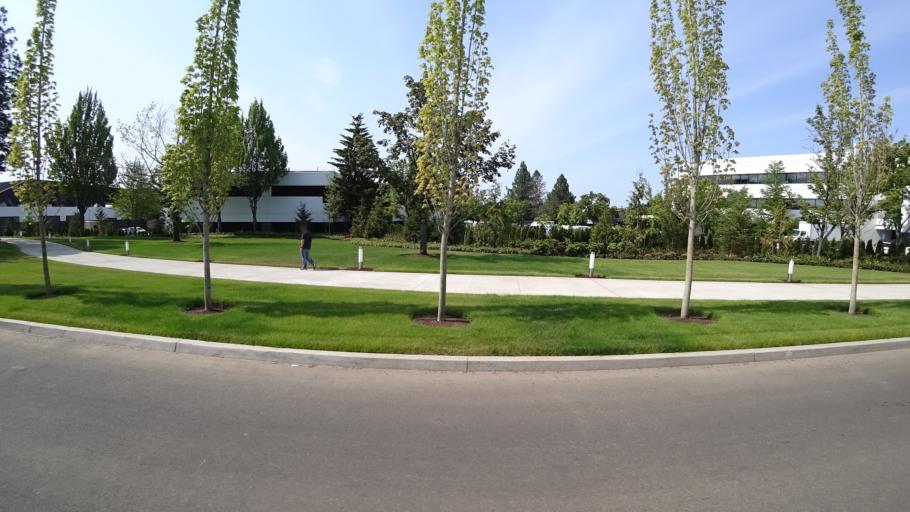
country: US
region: Oregon
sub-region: Washington County
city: Cedar Mill
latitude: 45.5147
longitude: -122.8344
